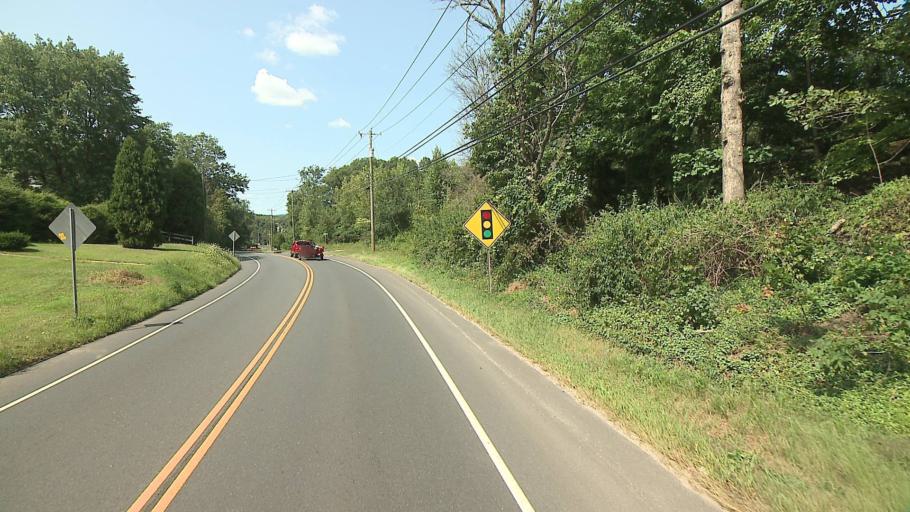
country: US
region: Connecticut
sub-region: Fairfield County
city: Newtown
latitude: 41.3586
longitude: -73.2643
